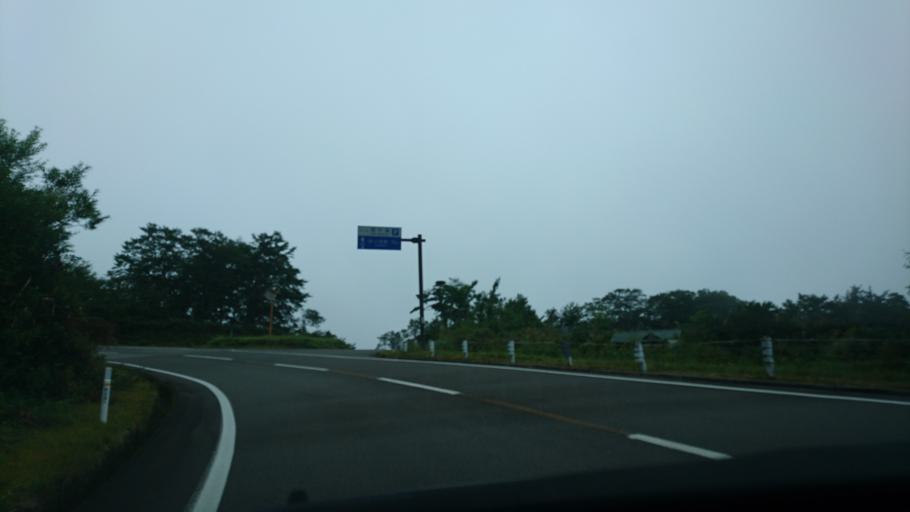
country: JP
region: Akita
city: Yuzawa
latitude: 38.9797
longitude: 140.7549
